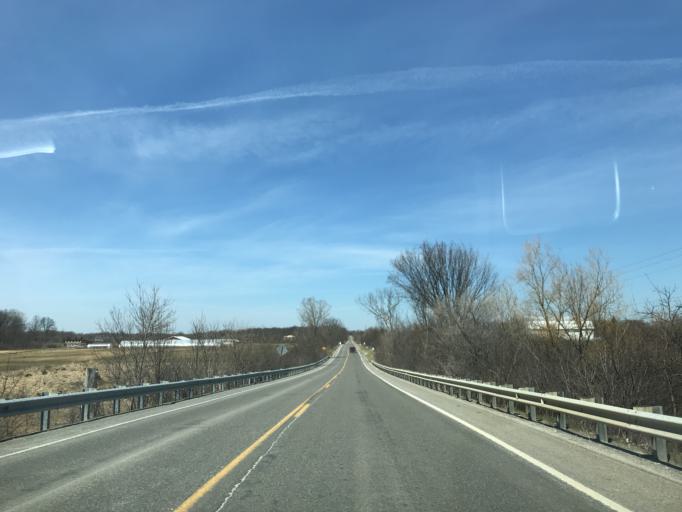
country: US
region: Michigan
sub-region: Washtenaw County
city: Ann Arbor
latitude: 42.3251
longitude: -83.7079
